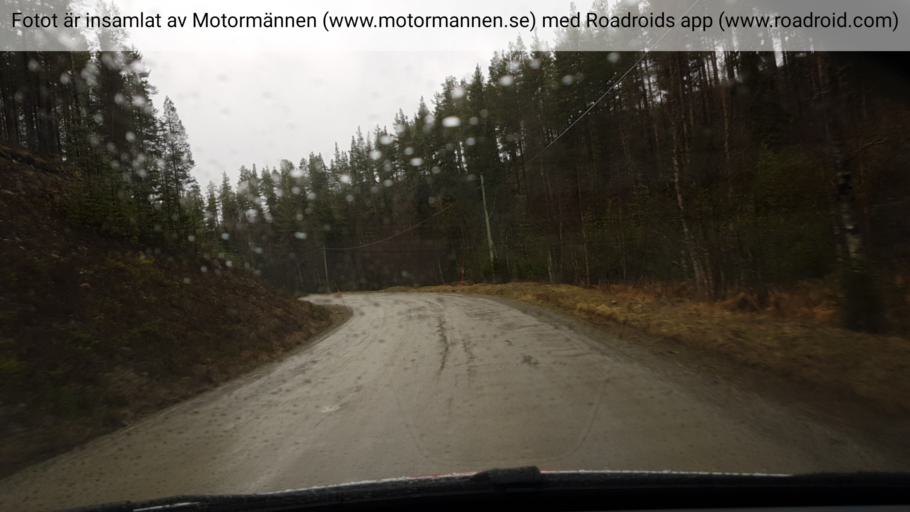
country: SE
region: Jaemtland
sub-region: Are Kommun
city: Jarpen
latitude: 62.4550
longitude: 13.5141
